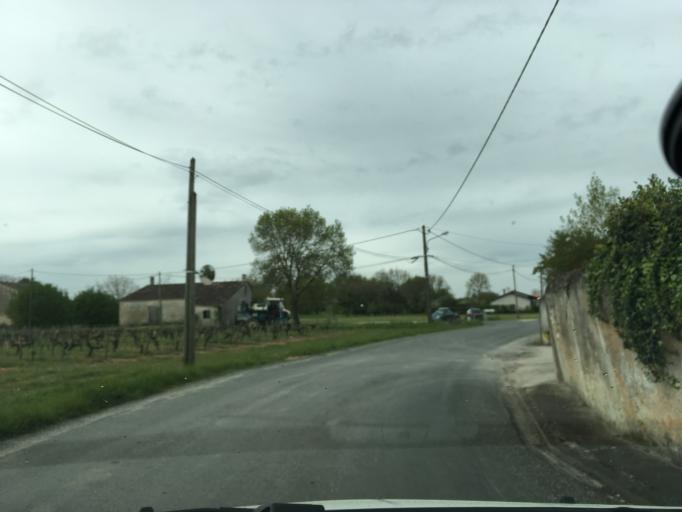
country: FR
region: Aquitaine
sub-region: Departement de la Gironde
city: Lesparre-Medoc
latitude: 45.3127
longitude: -0.8923
